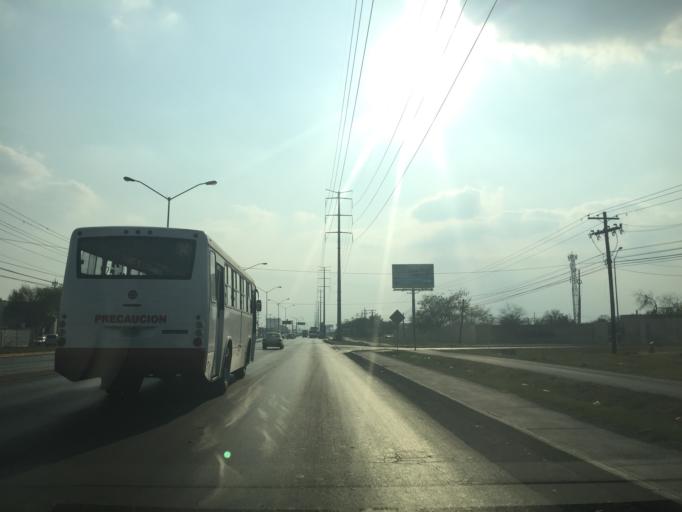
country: MX
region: Nuevo Leon
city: Apodaca
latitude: 25.7636
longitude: -100.2046
